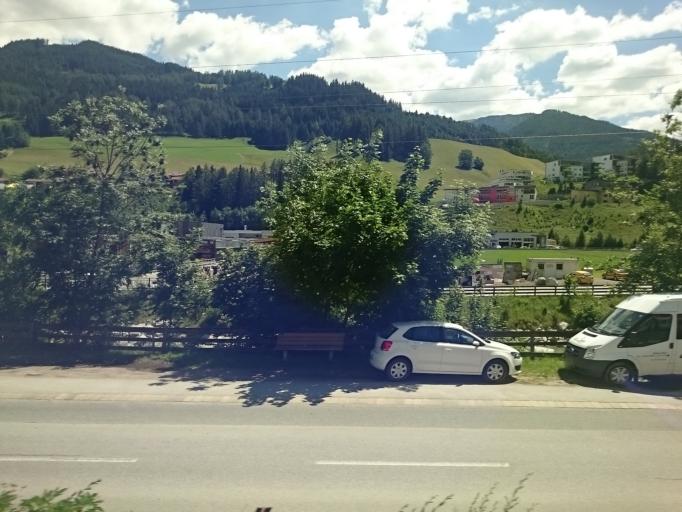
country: AT
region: Tyrol
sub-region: Politischer Bezirk Innsbruck Land
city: Matrei am Brenner
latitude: 47.1245
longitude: 11.4516
